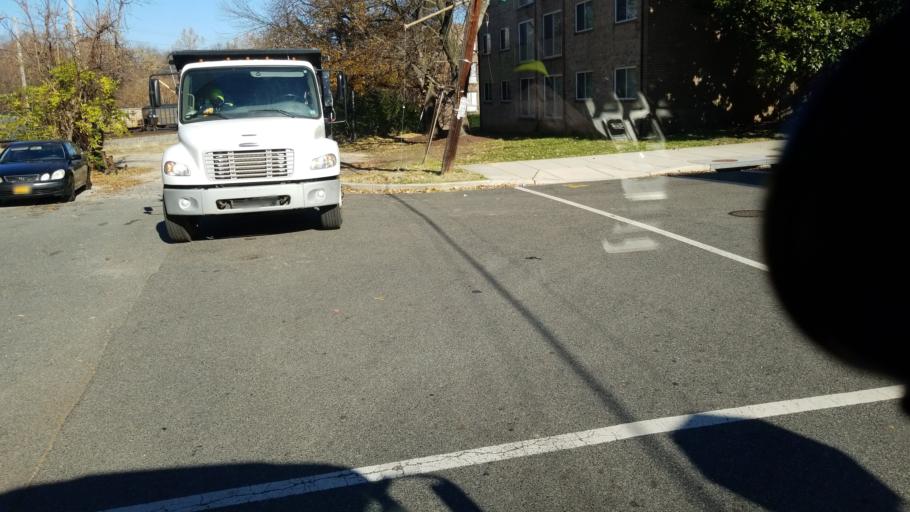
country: US
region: Maryland
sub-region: Prince George's County
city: Coral Hills
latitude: 38.8859
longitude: -76.9598
